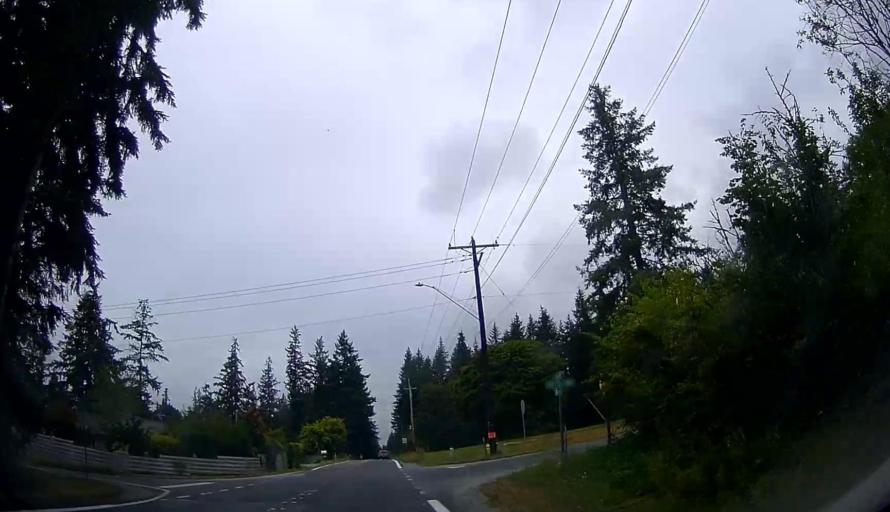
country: US
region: Washington
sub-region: Snohomish County
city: Warm Beach
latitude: 48.1595
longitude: -122.3576
